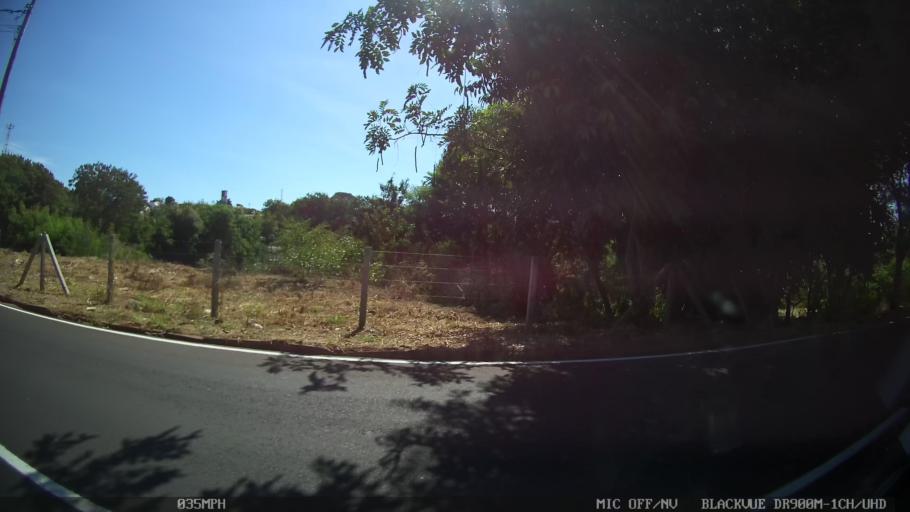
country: BR
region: Sao Paulo
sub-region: Sao Jose Do Rio Preto
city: Sao Jose do Rio Preto
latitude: -20.7738
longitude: -49.4075
